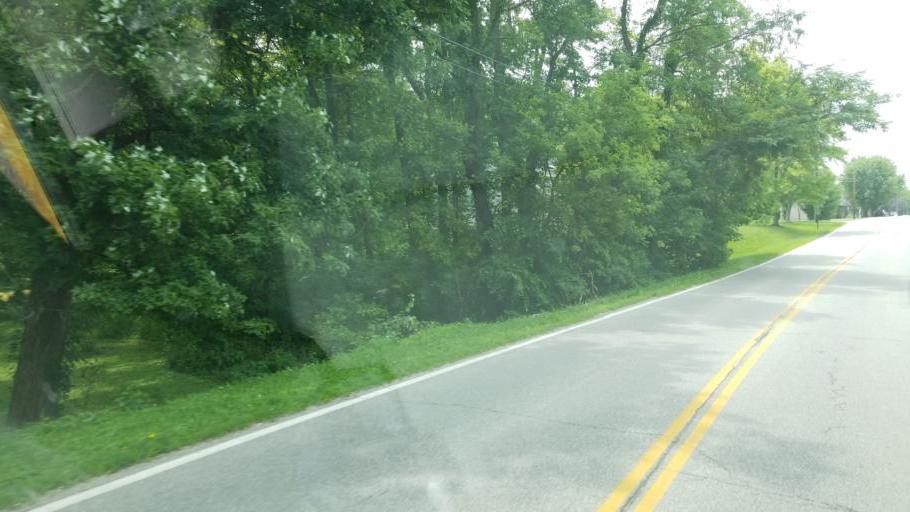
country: US
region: Ohio
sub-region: Madison County
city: Plain City
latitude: 40.0683
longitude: -83.2513
